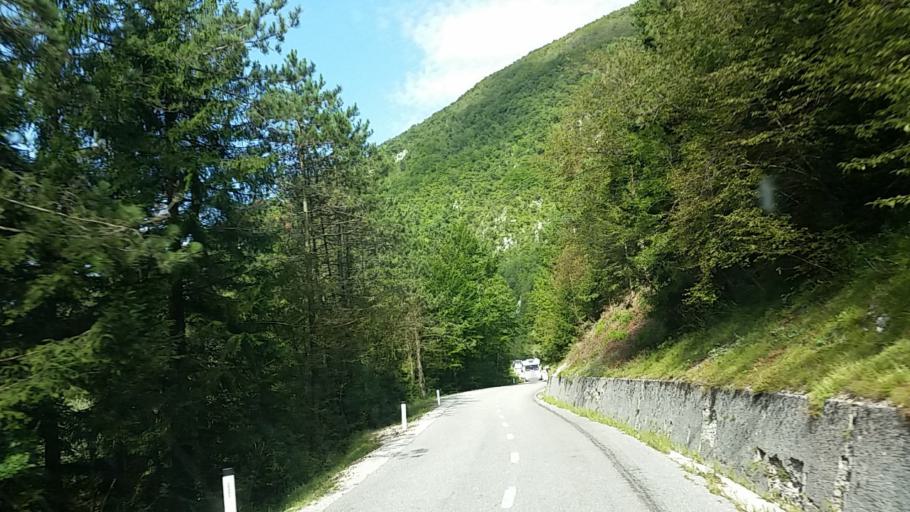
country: SI
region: Bovec
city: Bovec
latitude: 46.3378
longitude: 13.6050
